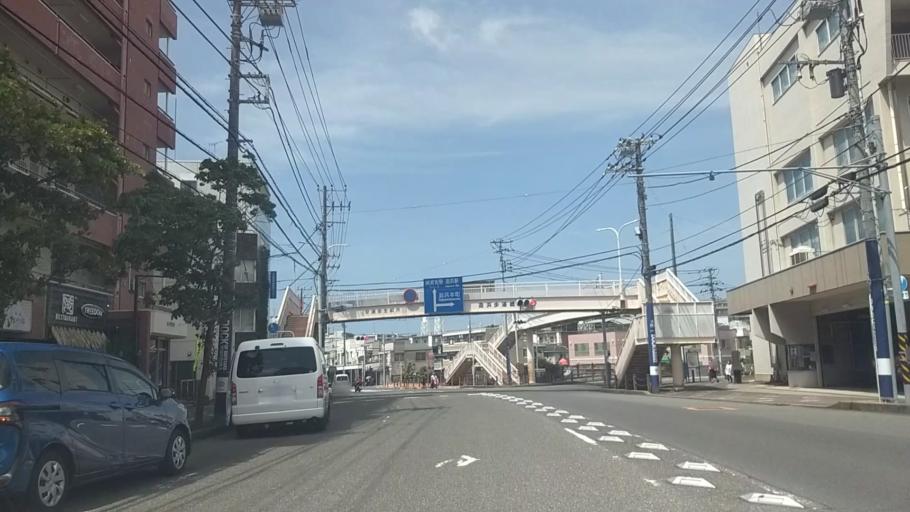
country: JP
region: Kanagawa
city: Yokosuka
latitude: 35.3173
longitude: 139.6316
